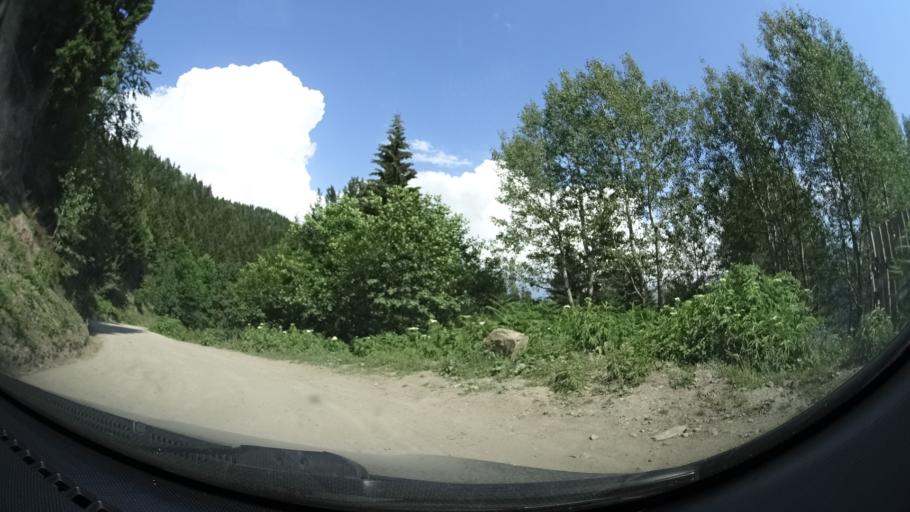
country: GE
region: Ajaria
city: Dioknisi
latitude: 41.6491
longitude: 42.4695
